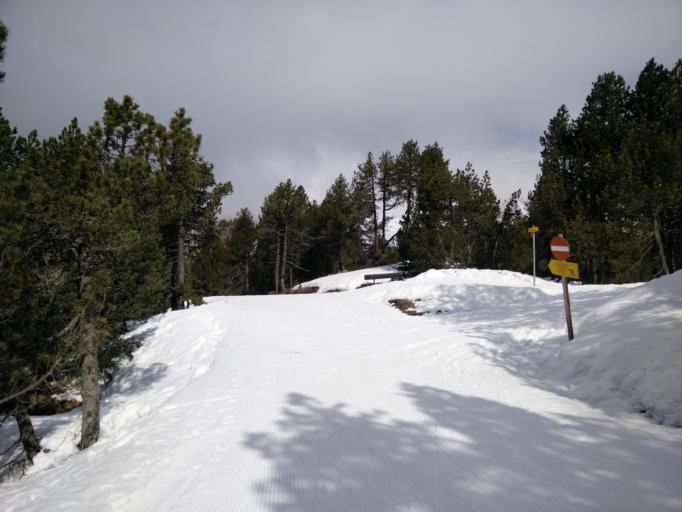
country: CH
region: Grisons
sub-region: Maloja District
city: Silvaplana
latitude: 46.4005
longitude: 9.6999
